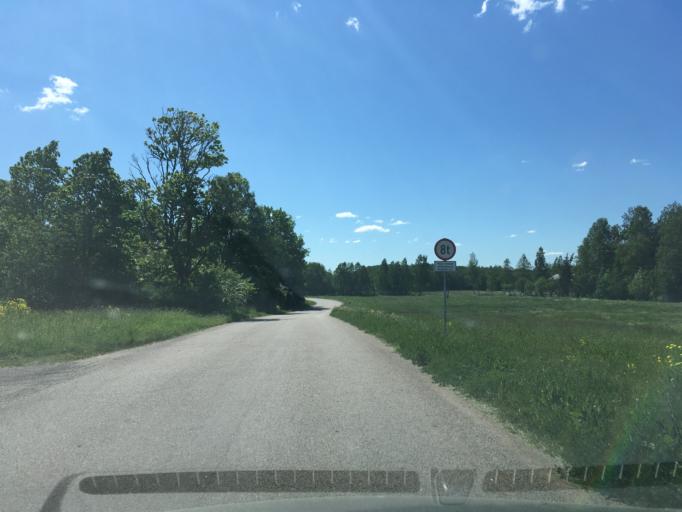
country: EE
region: Harju
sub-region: Rae vald
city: Vaida
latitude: 59.1776
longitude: 25.1202
